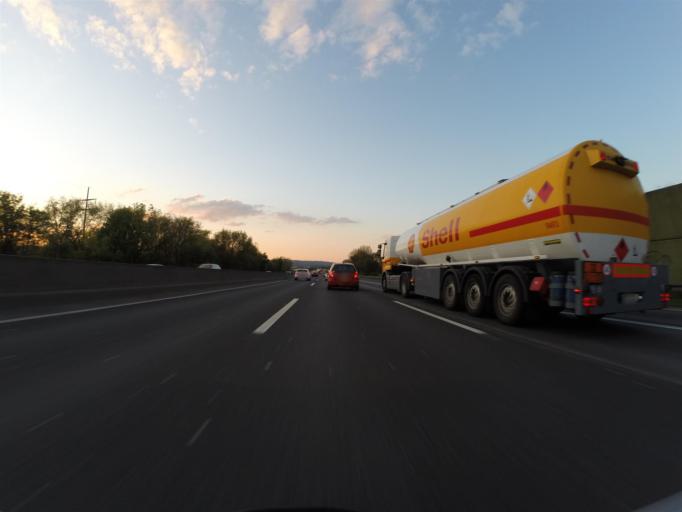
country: DE
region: Hesse
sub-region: Regierungsbezirk Darmstadt
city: Friedrichsdorf
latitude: 50.2327
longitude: 8.6632
